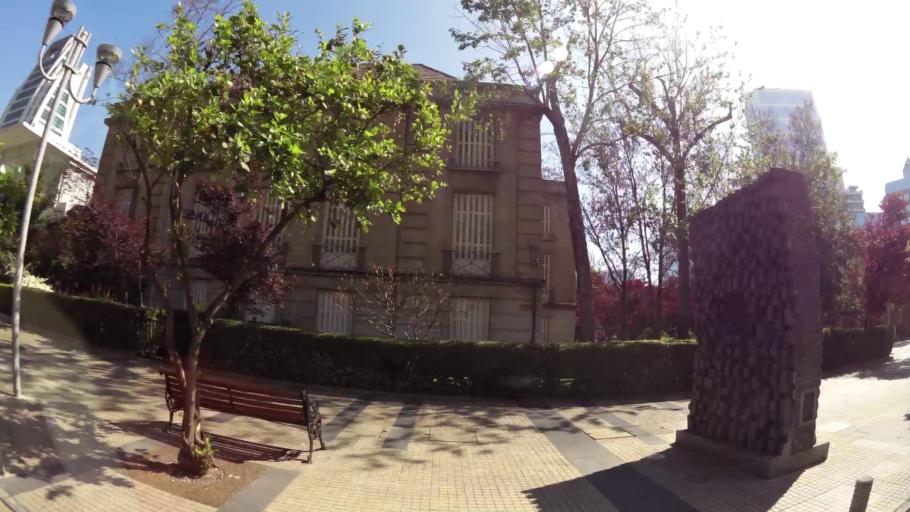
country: CL
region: Santiago Metropolitan
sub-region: Provincia de Santiago
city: Villa Presidente Frei, Nunoa, Santiago, Chile
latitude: -33.4150
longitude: -70.5962
